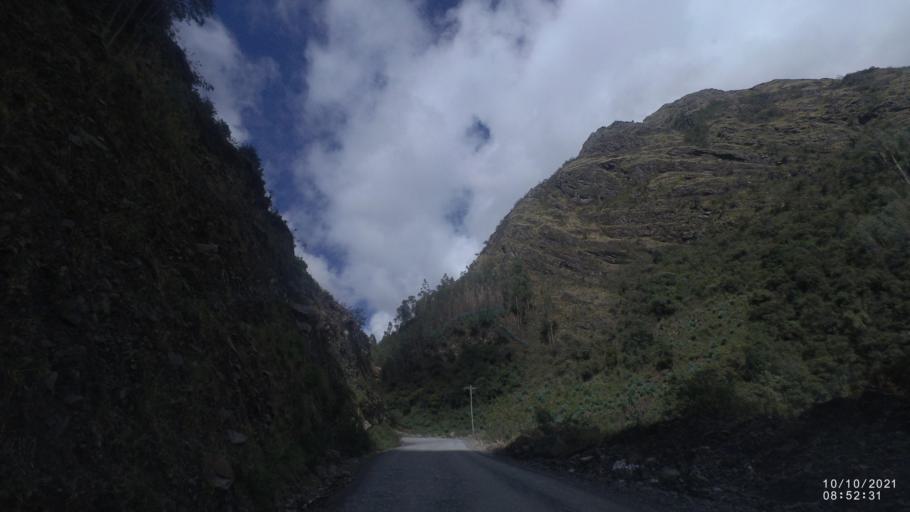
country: BO
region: La Paz
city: Quime
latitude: -16.9855
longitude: -67.2286
